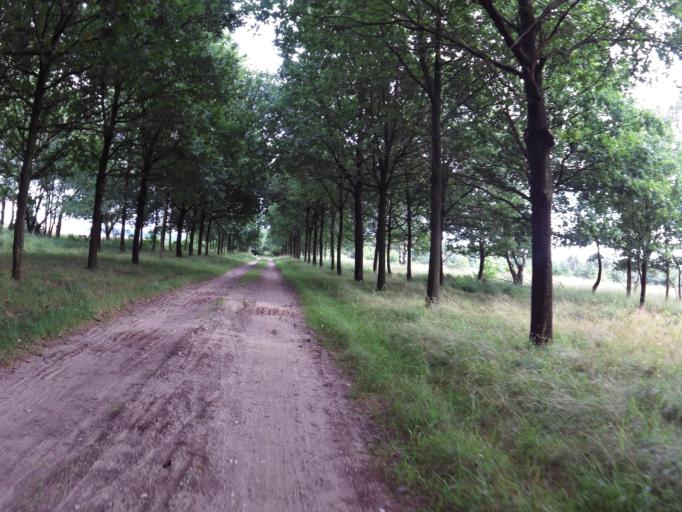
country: NL
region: Gelderland
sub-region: Gemeente Arnhem
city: Gulden Bodem
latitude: 52.0534
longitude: 5.9131
